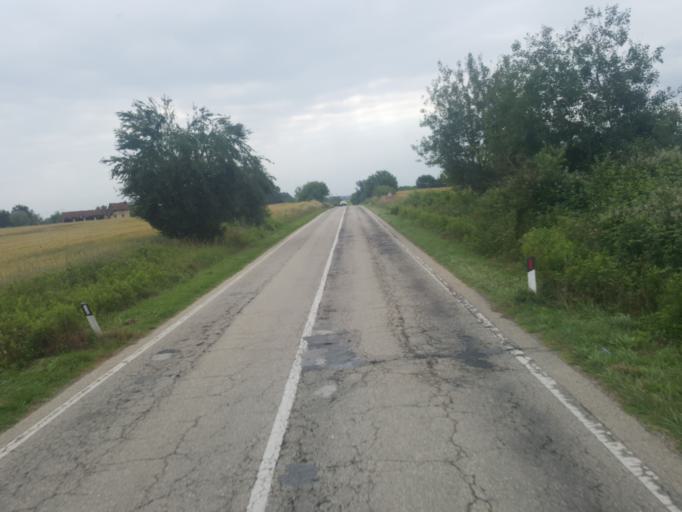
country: IT
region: Piedmont
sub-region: Provincia di Torino
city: Pralormo
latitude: 44.8528
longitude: 7.8549
